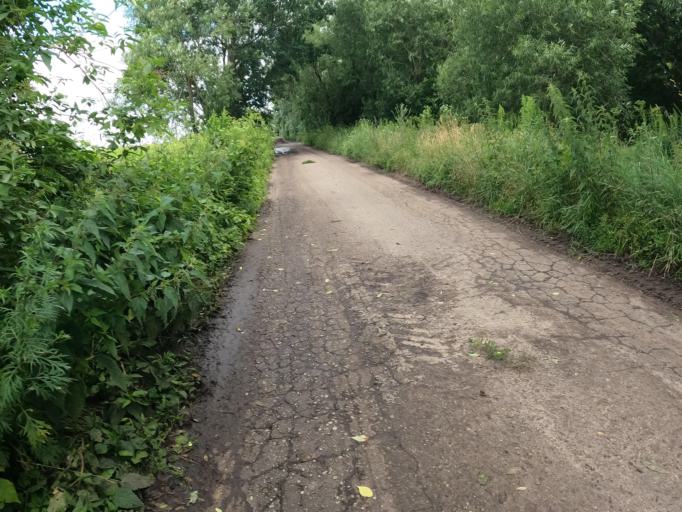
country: PL
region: West Pomeranian Voivodeship
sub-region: Powiat bialogardzki
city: Bialogard
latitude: 54.0011
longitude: 15.9505
